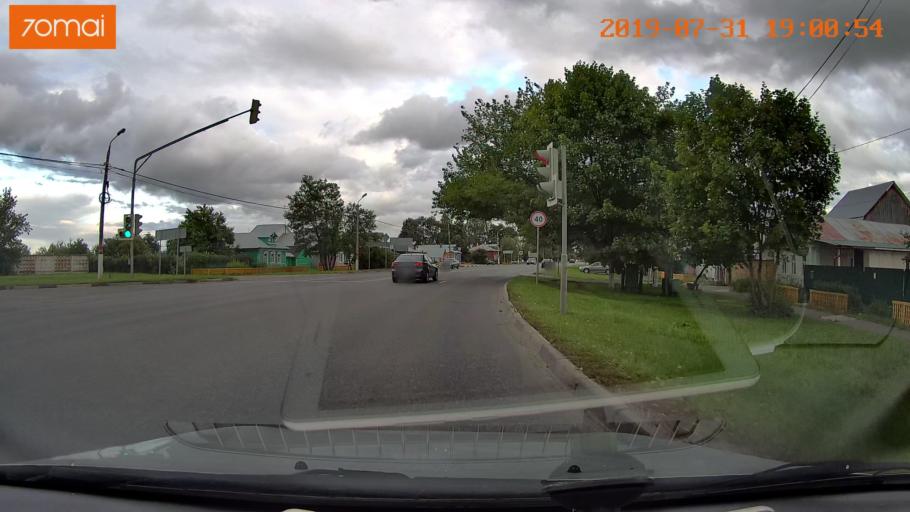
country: RU
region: Moskovskaya
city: Raduzhnyy
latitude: 55.1304
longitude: 38.7278
